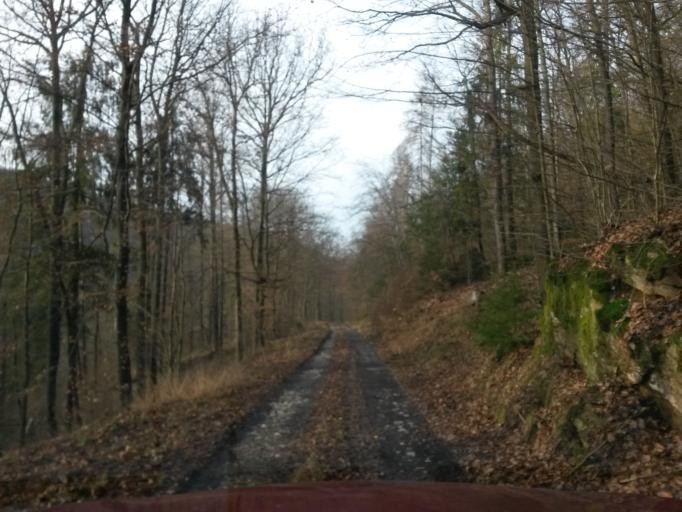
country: SK
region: Kosicky
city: Dobsina
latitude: 48.7303
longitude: 20.4039
